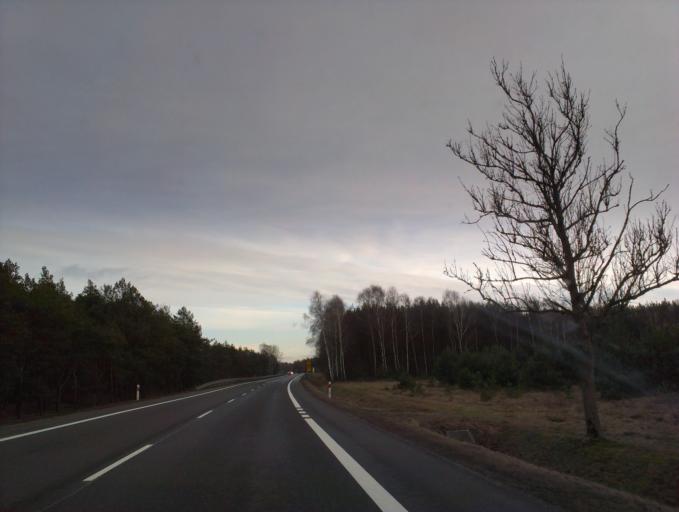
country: PL
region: Masovian Voivodeship
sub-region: Powiat sierpecki
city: Szczutowo
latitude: 52.8939
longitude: 19.5540
